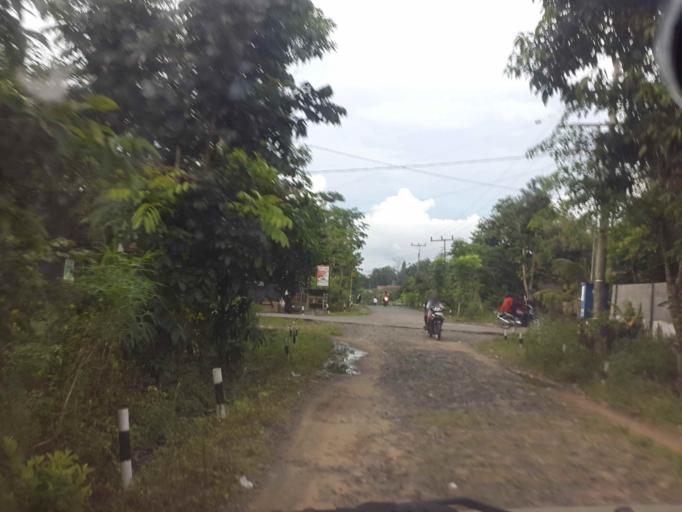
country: ID
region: Lampung
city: Sidorejo
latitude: -5.5391
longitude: 105.5706
